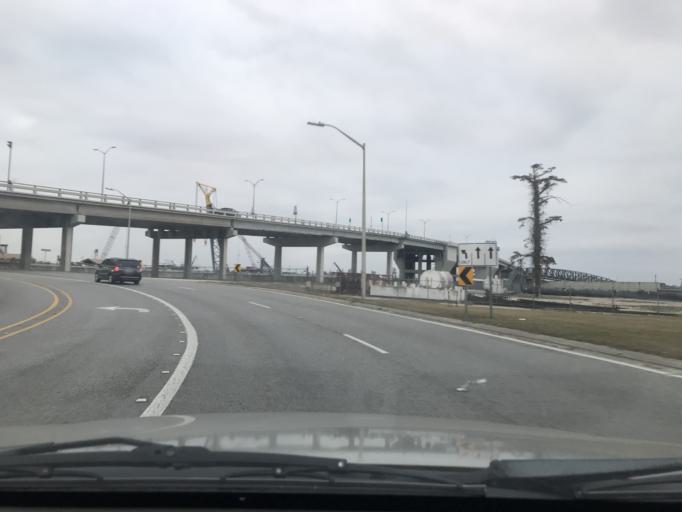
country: US
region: Louisiana
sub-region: Jefferson Parish
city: Woodmere
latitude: 29.8699
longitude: -90.0720
